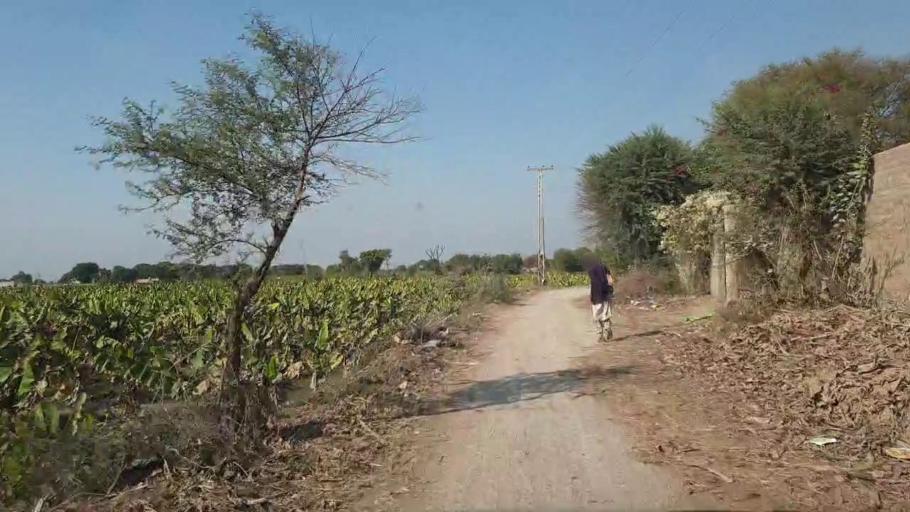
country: PK
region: Sindh
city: Chambar
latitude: 25.3250
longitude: 68.7578
